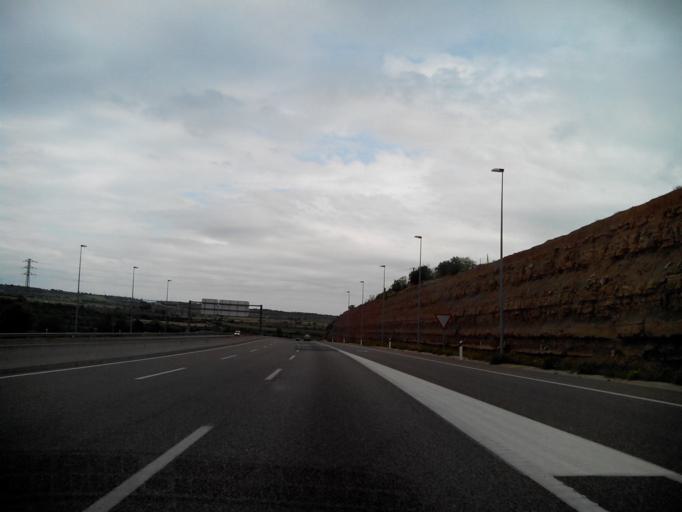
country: ES
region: Catalonia
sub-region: Provincia de Lleida
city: Cervera
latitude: 41.6837
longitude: 1.2453
